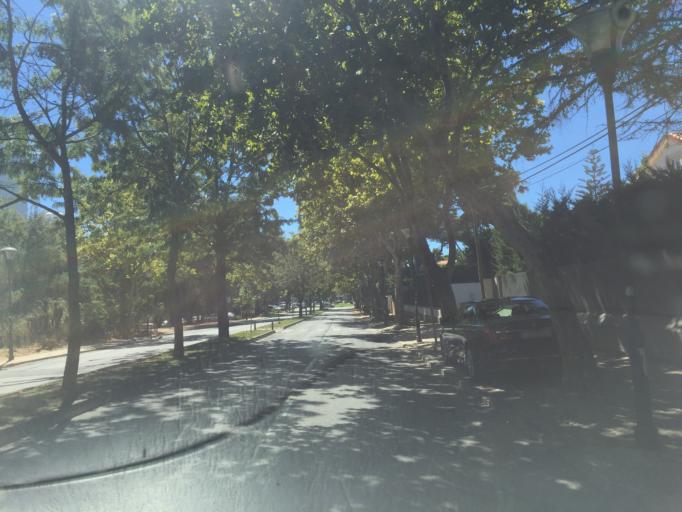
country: PT
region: Lisbon
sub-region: Cascais
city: Cascais
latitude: 38.6990
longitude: -9.4323
